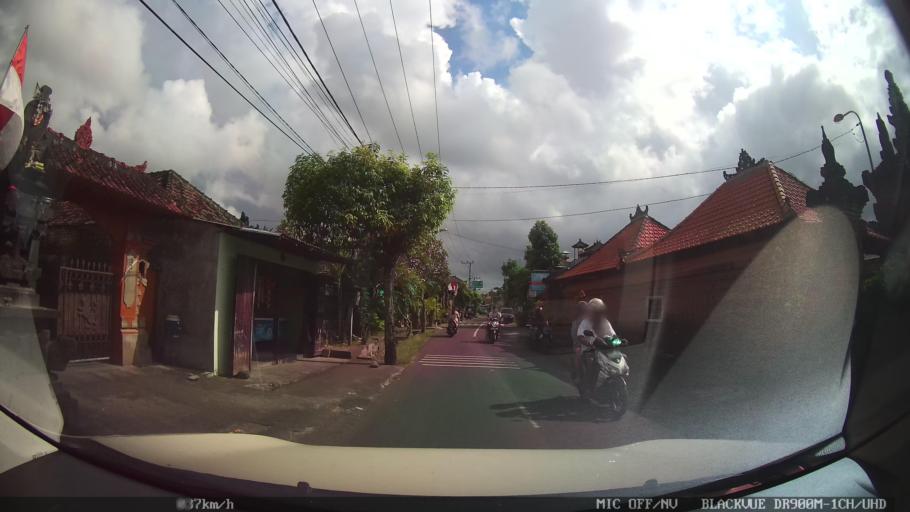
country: ID
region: Bali
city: Banjar Karangsuling
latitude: -8.6126
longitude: 115.1996
